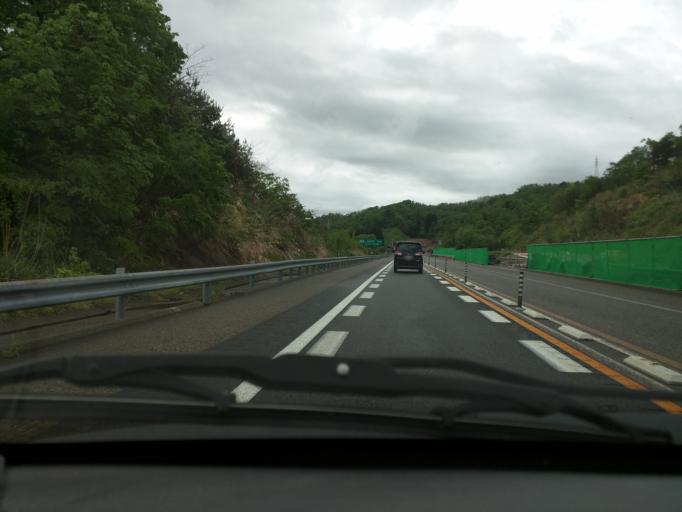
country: JP
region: Niigata
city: Joetsu
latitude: 37.1122
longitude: 138.2188
